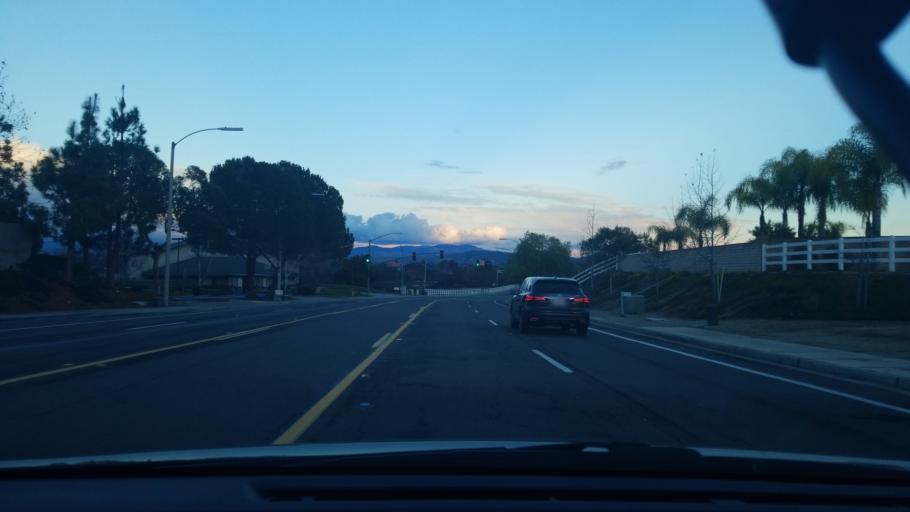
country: US
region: California
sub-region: Riverside County
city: Temecula
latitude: 33.4966
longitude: -117.1229
